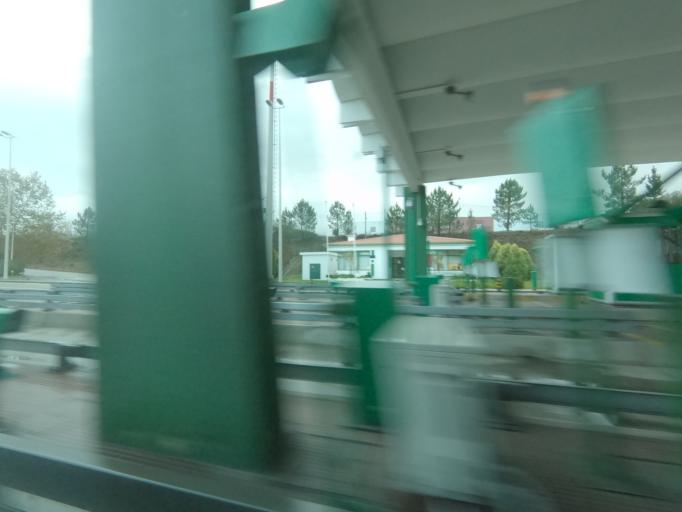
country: PT
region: Viana do Castelo
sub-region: Valenca
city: Valenza
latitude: 41.9788
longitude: -8.6542
